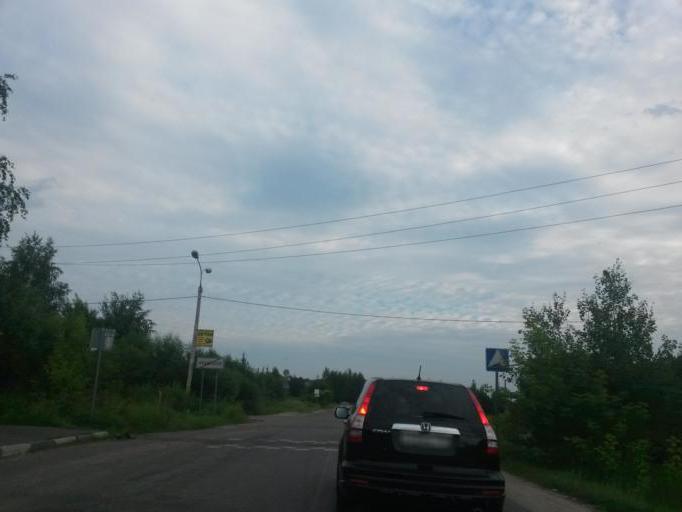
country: RU
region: Moskovskaya
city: Lyubuchany
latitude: 55.2719
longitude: 37.6221
